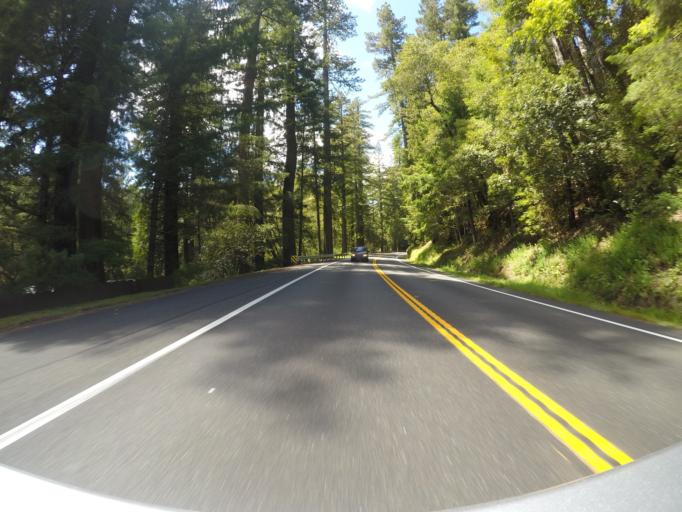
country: US
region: California
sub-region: Humboldt County
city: Redway
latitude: 39.9164
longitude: -123.7662
